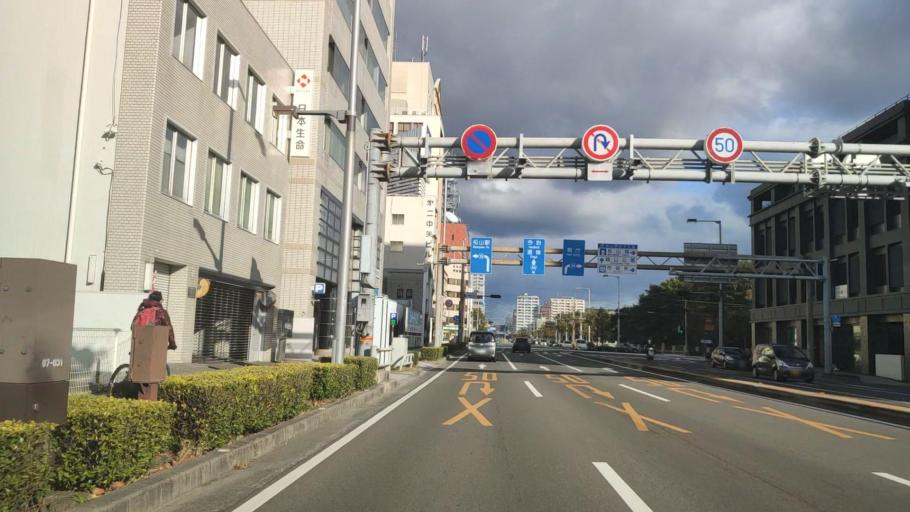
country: JP
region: Ehime
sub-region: Shikoku-chuo Shi
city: Matsuyama
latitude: 33.8386
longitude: 132.7587
